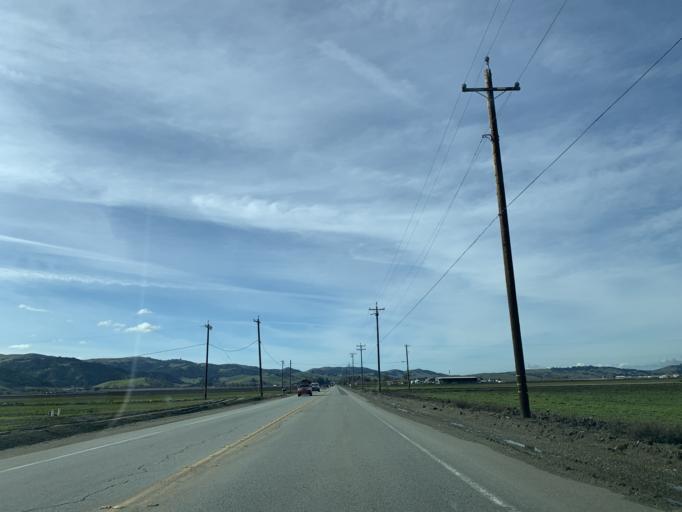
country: US
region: California
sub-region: San Benito County
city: San Juan Bautista
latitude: 36.8416
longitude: -121.4936
